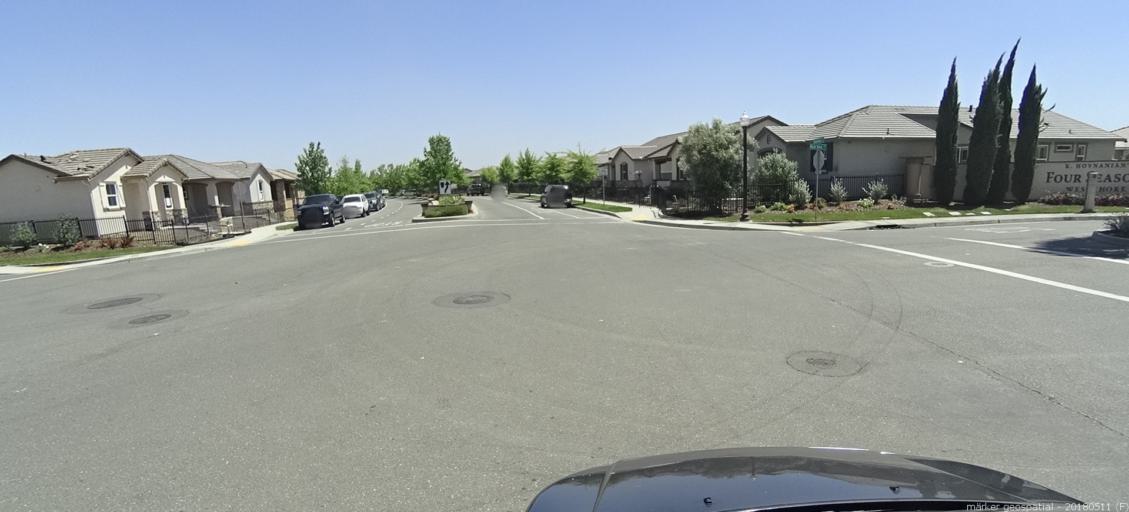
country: US
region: California
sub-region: Yolo County
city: West Sacramento
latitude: 38.6531
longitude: -121.5510
